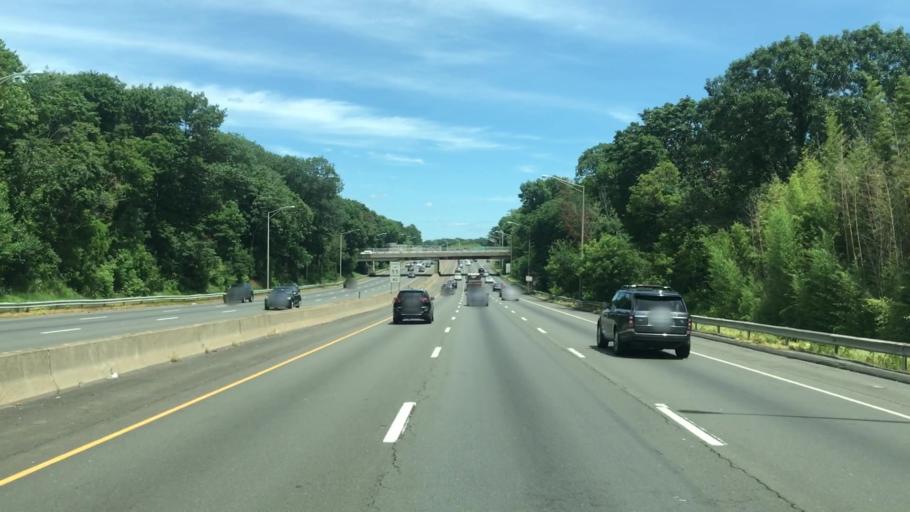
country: US
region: Connecticut
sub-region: Fairfield County
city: Pemberwick
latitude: 41.0298
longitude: -73.6713
